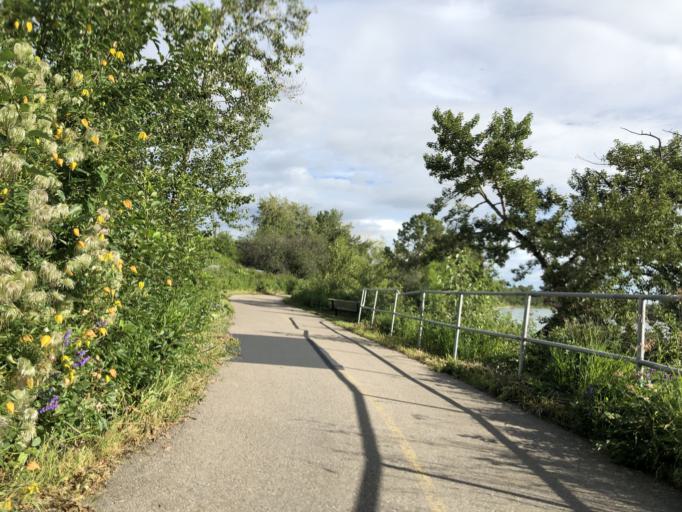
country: CA
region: Alberta
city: Calgary
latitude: 51.0158
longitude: -114.0124
